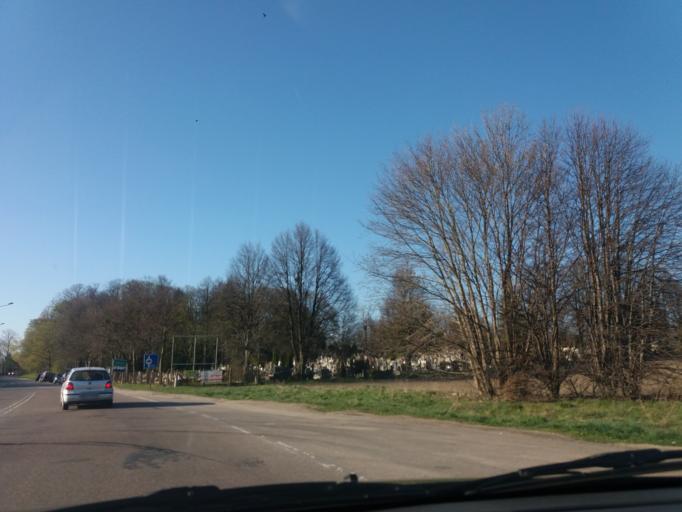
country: PL
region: Warmian-Masurian Voivodeship
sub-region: Powiat nidzicki
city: Nidzica
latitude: 53.3481
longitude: 20.4312
